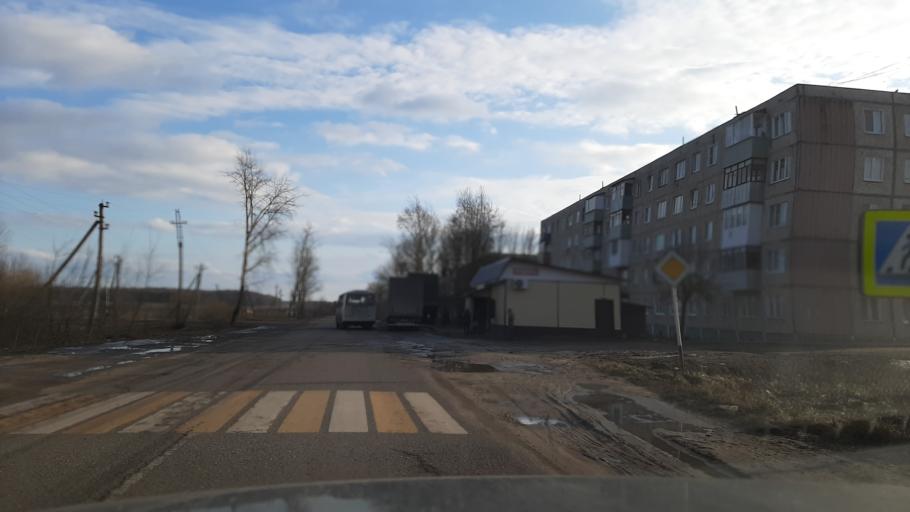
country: RU
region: Ivanovo
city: Novo-Talitsy
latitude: 56.9238
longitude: 40.7382
